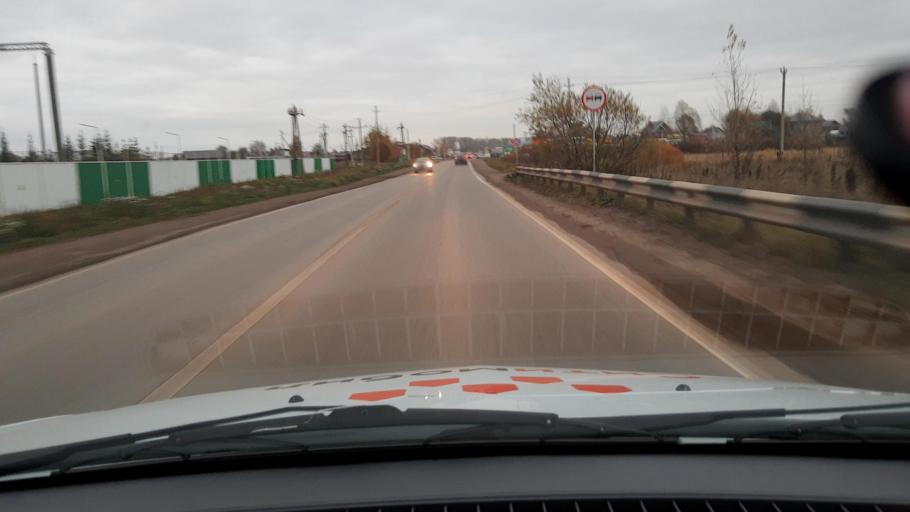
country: RU
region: Bashkortostan
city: Ufa
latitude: 54.6720
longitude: 56.0843
